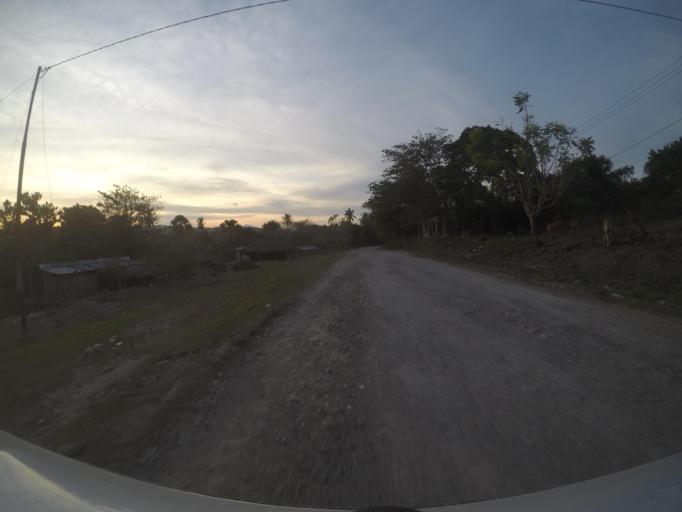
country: TL
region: Viqueque
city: Viqueque
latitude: -8.9226
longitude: 126.3978
